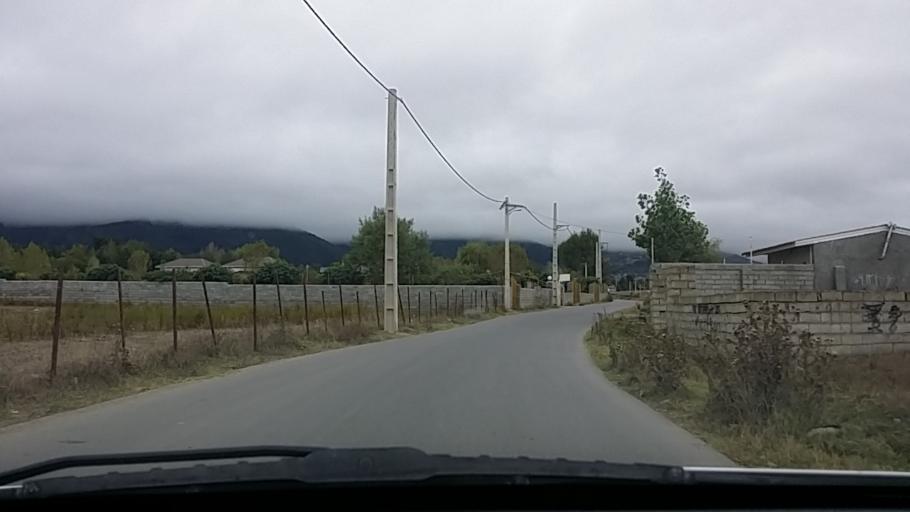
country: IR
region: Mazandaran
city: `Abbasabad
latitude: 36.5209
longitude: 51.1706
